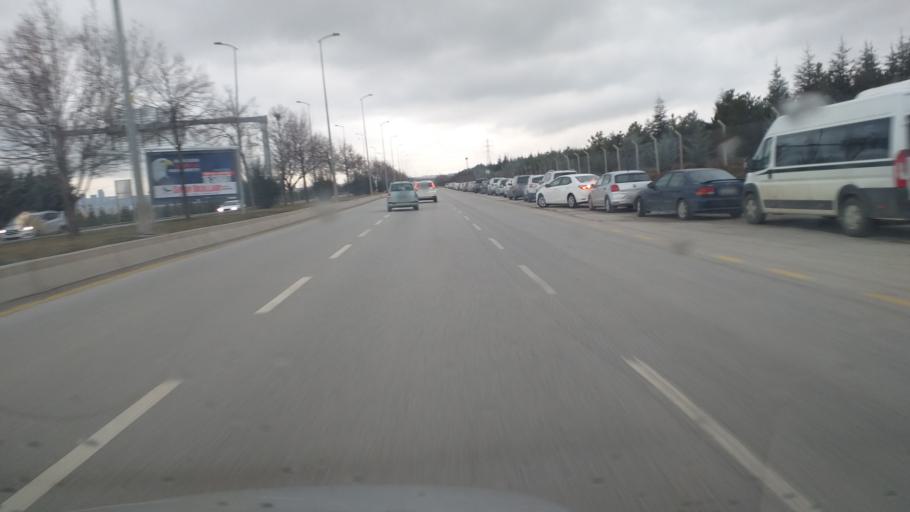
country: TR
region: Ankara
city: Batikent
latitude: 39.9041
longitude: 32.7327
